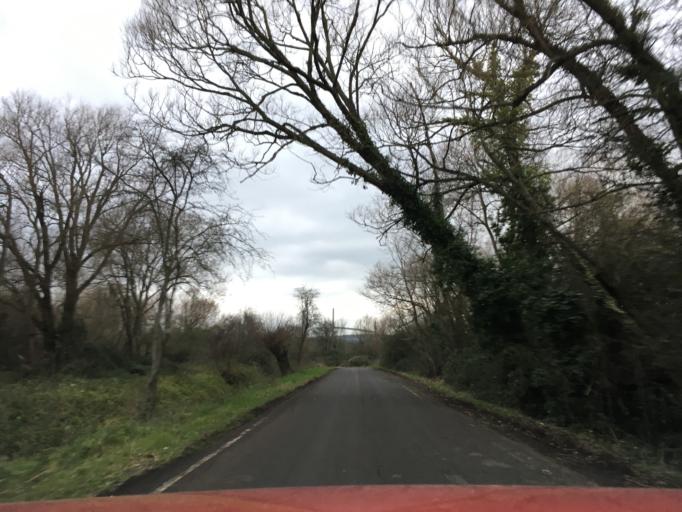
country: GB
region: Wales
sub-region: Newport
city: Bishton
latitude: 51.5783
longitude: -2.8713
